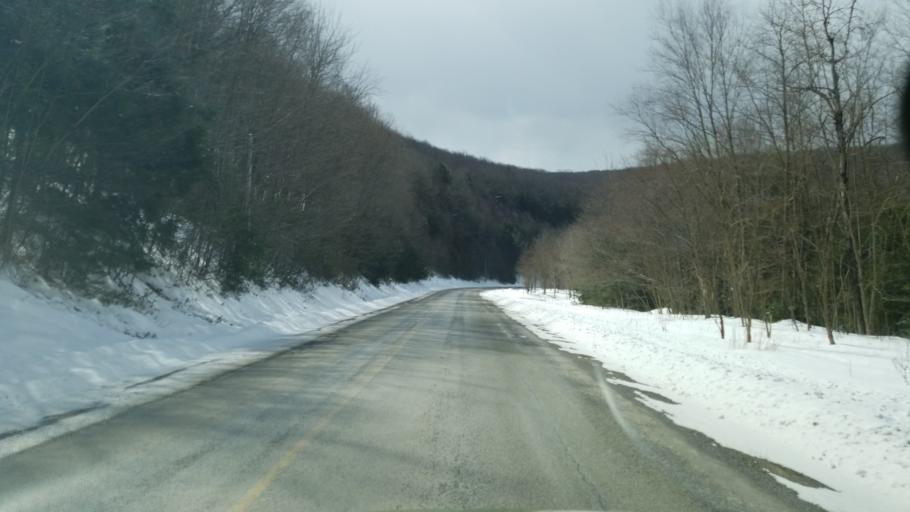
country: US
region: Pennsylvania
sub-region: Clearfield County
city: Shiloh
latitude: 41.2515
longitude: -78.3731
